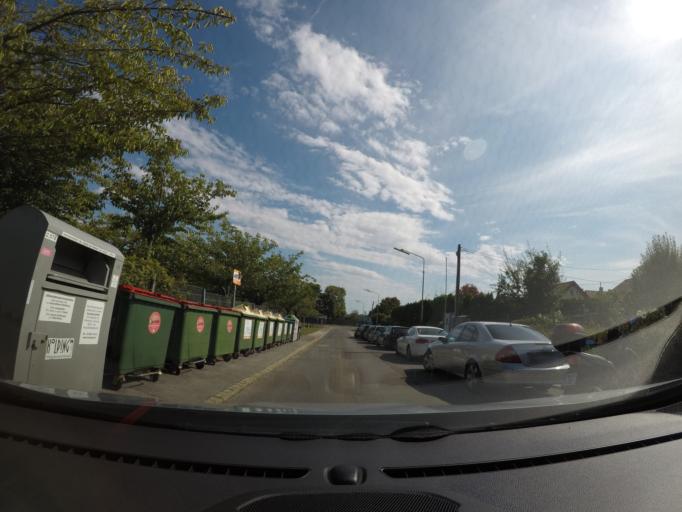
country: AT
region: Lower Austria
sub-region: Politischer Bezirk Modling
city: Perchtoldsdorf
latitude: 48.2053
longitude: 16.2810
